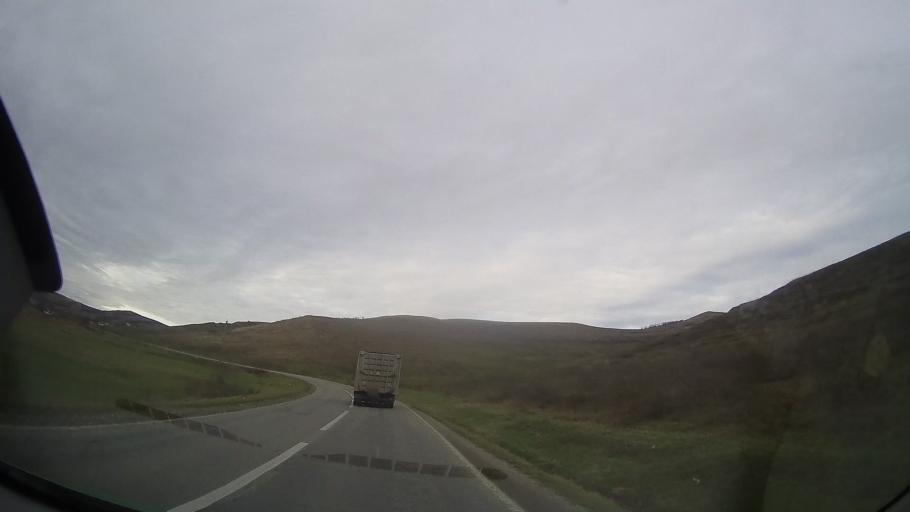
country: RO
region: Cluj
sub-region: Comuna Camarasu
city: Camarasu
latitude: 46.8024
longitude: 24.1599
